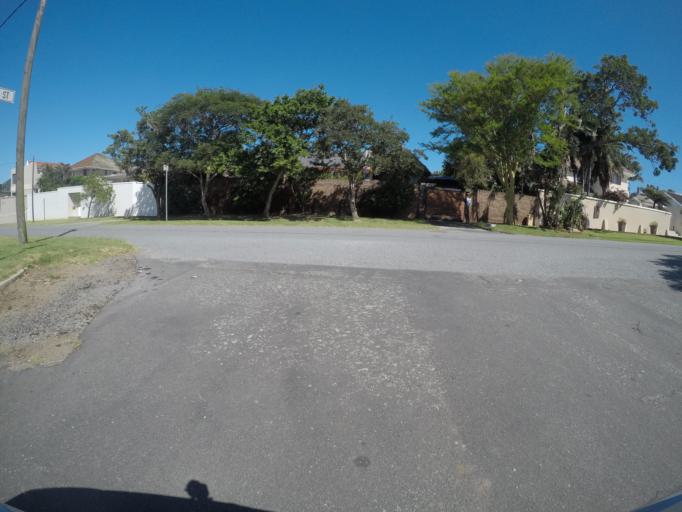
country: ZA
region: Eastern Cape
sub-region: Buffalo City Metropolitan Municipality
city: East London
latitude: -32.9861
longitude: 27.9431
